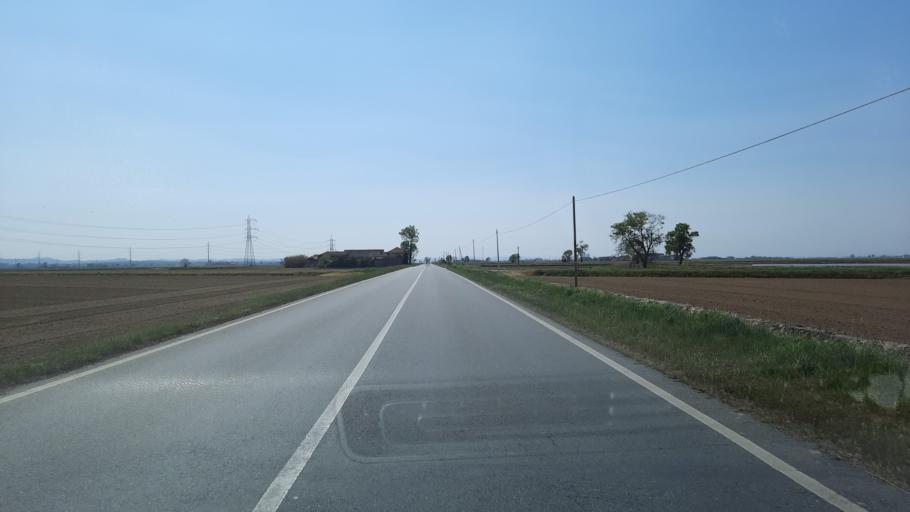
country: IT
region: Piedmont
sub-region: Provincia di Vercelli
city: Lignana
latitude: 45.2780
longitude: 8.3194
